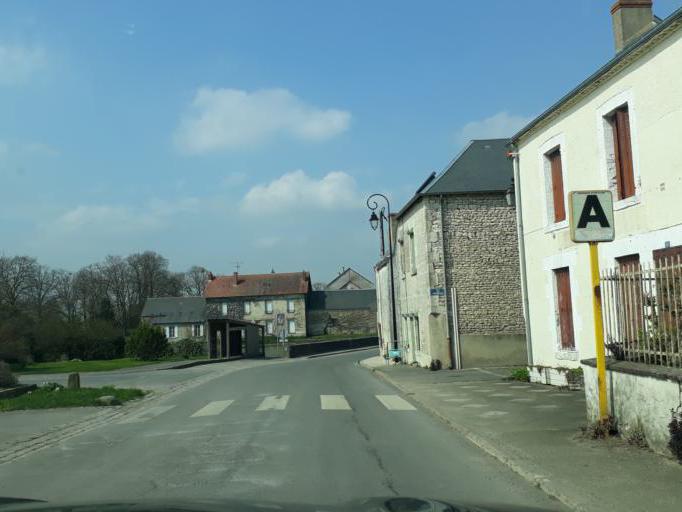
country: FR
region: Centre
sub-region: Departement d'Eure-et-Loir
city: Baigneaux
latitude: 48.0995
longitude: 1.8396
